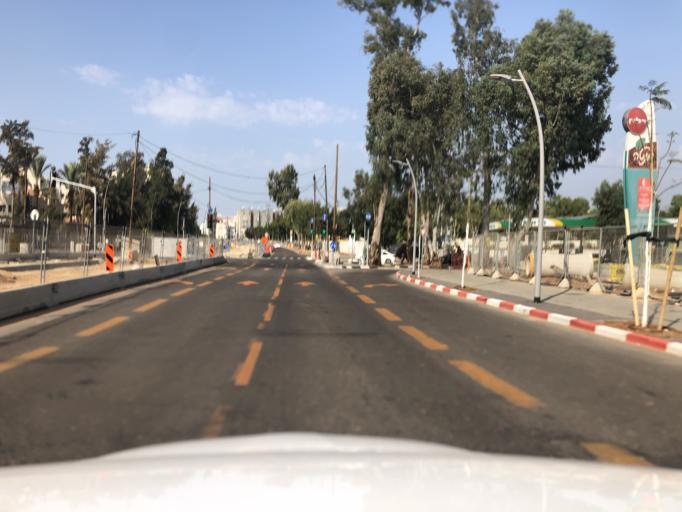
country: IL
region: Central District
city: Kfar Saba
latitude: 32.1710
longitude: 34.9248
